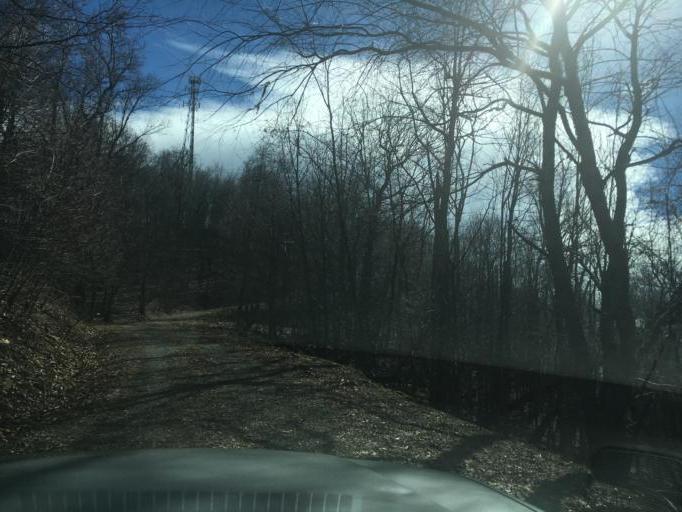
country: US
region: North Carolina
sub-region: Haywood County
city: Canton
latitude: 35.4690
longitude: -82.8297
